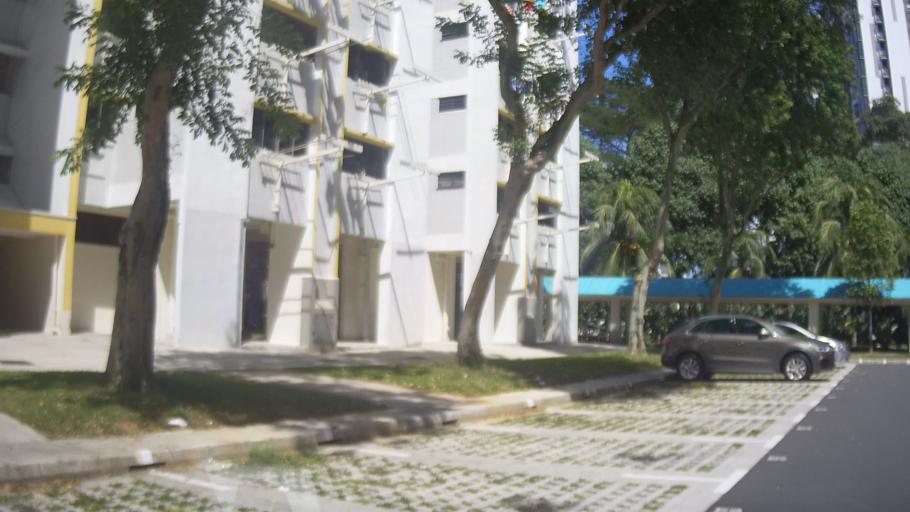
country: SG
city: Singapore
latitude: 1.3193
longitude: 103.8827
